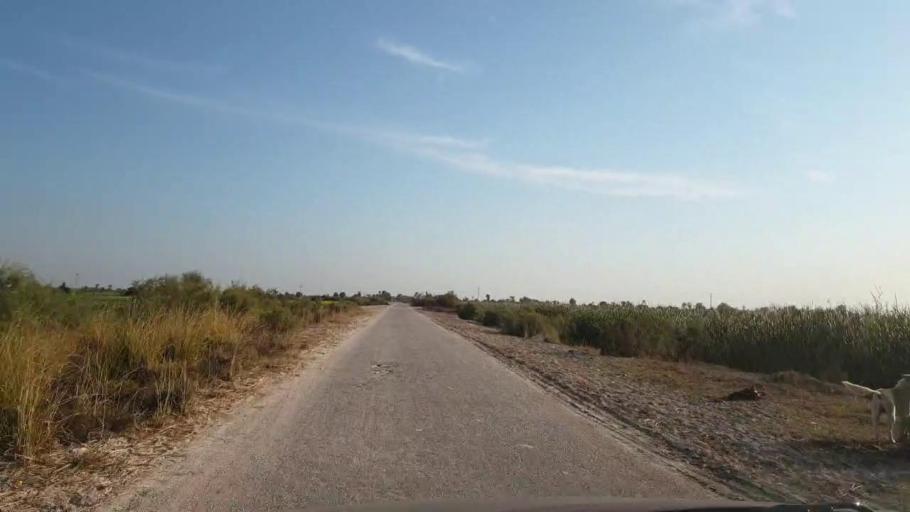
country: PK
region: Sindh
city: Khadro
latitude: 26.2079
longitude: 68.7458
